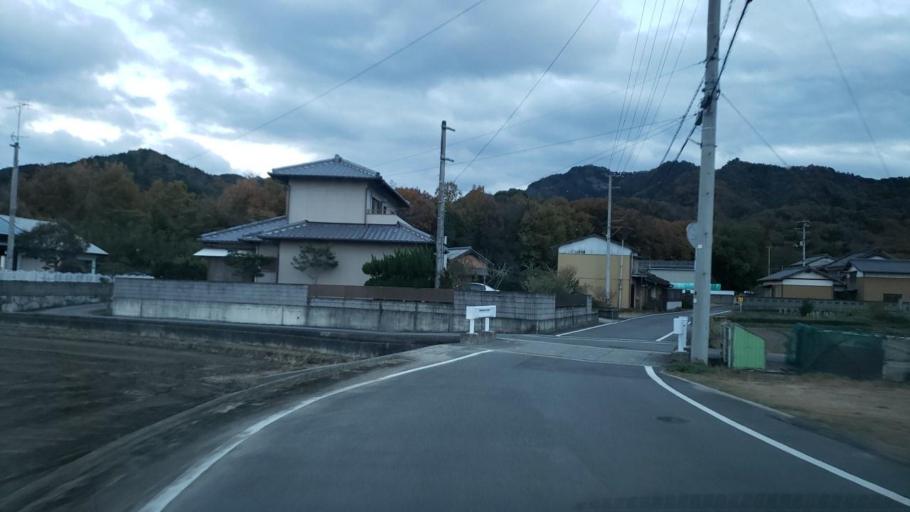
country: JP
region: Tokushima
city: Kamojimacho-jogejima
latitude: 34.2337
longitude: 134.3466
